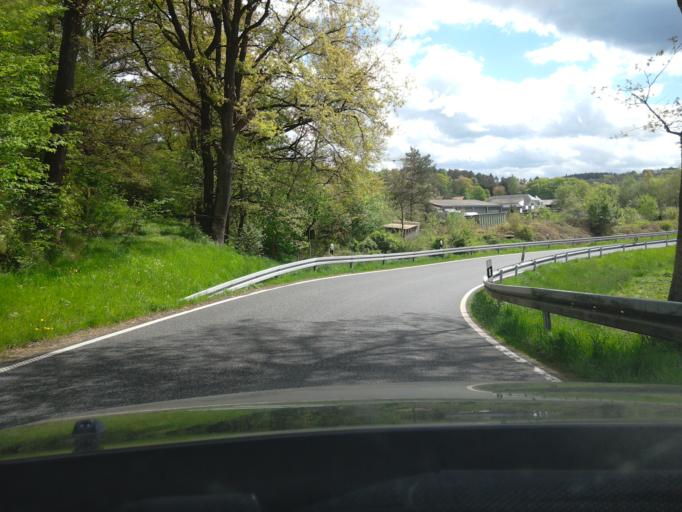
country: DE
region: Bavaria
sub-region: Regierungsbezirk Unterfranken
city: Aura im Sinngrund
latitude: 50.2116
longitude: 9.4891
